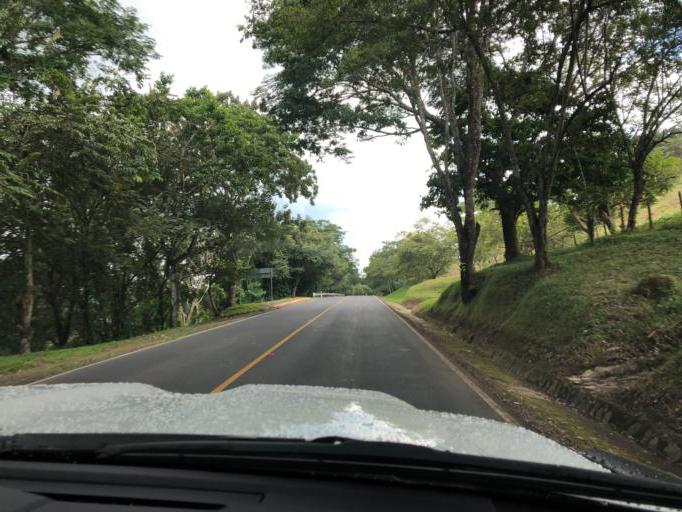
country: NI
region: Chontales
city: Villa Sandino
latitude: 11.9960
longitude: -84.9297
